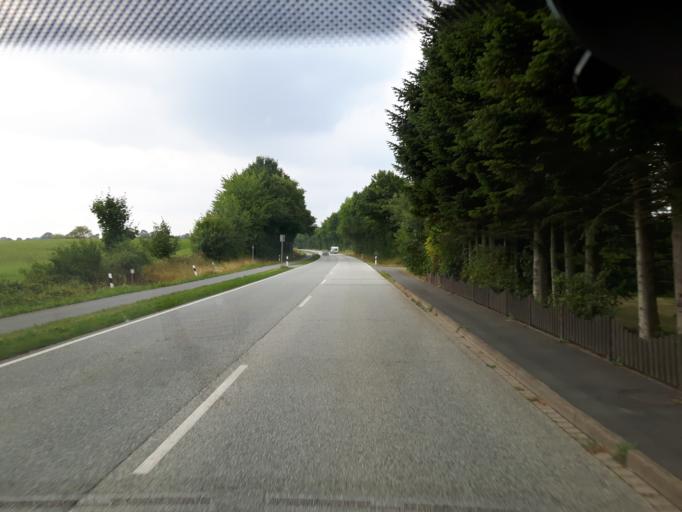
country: DE
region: Schleswig-Holstein
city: Holzbunge
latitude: 54.3747
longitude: 9.7033
